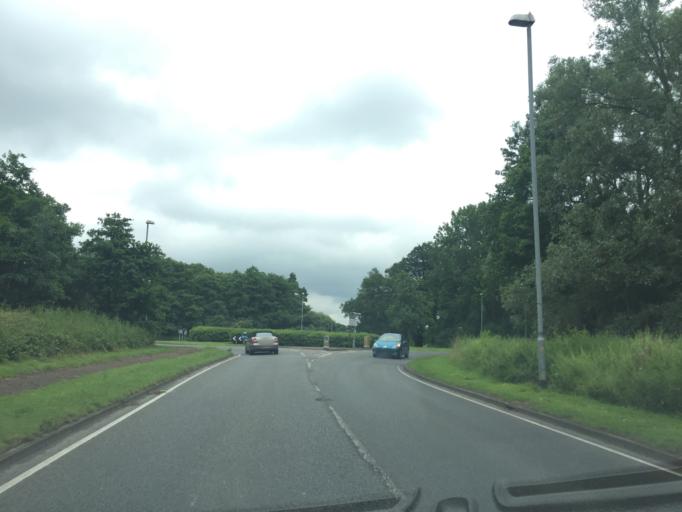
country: GB
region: England
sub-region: Greater London
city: Collier Row
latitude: 51.6553
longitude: 0.1708
